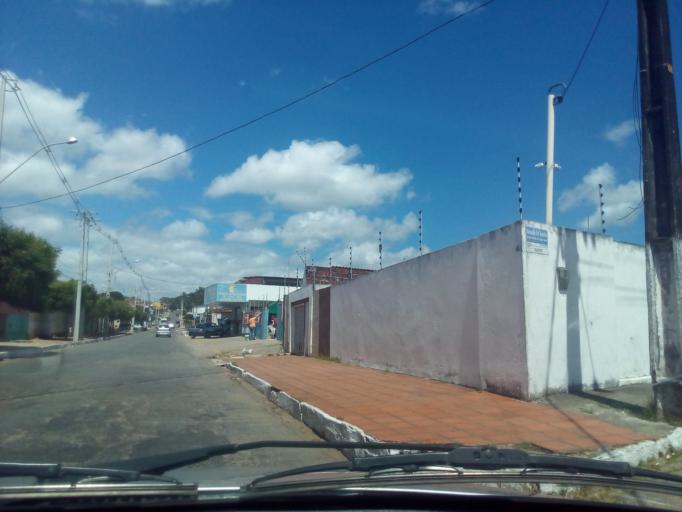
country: BR
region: Rio Grande do Norte
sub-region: Sao Goncalo Do Amarante
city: Sao Goncalo do Amarante
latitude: -5.7911
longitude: -35.3322
